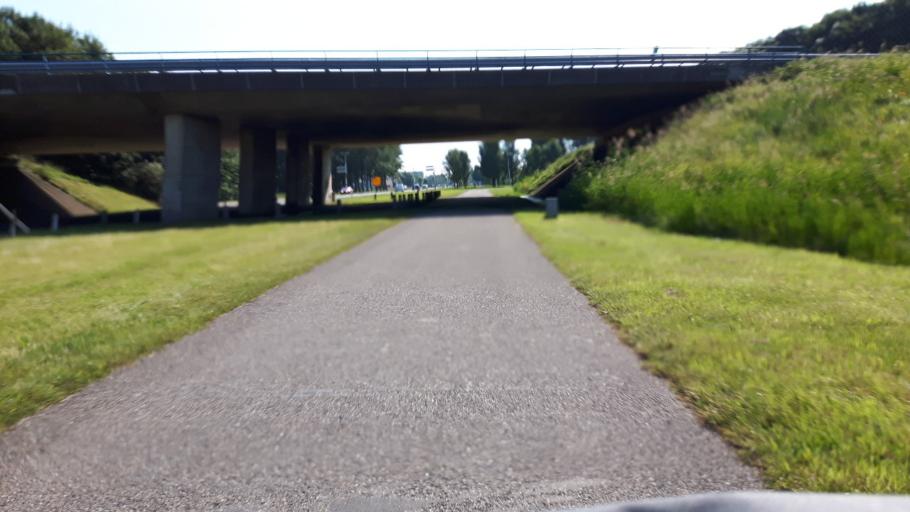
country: NL
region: Friesland
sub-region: Gemeente Franekeradeel
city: Franeker
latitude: 53.2010
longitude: 5.5414
